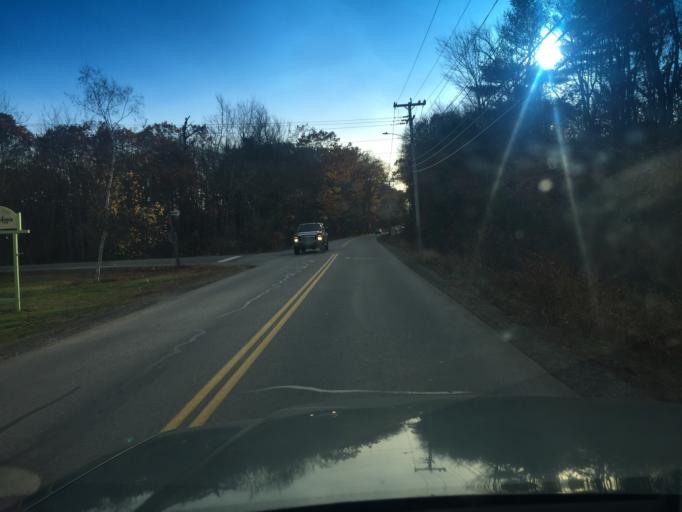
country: US
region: Maine
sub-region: York County
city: York Beach
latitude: 43.1594
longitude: -70.6299
